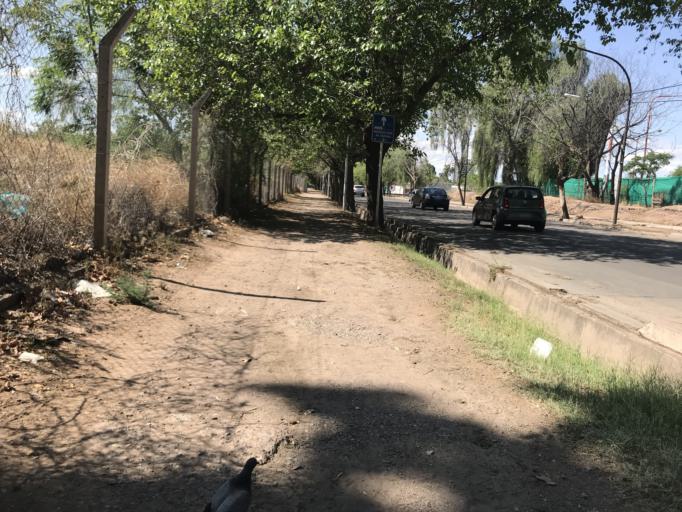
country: AR
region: Mendoza
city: Mendoza
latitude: -32.8798
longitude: -68.8393
